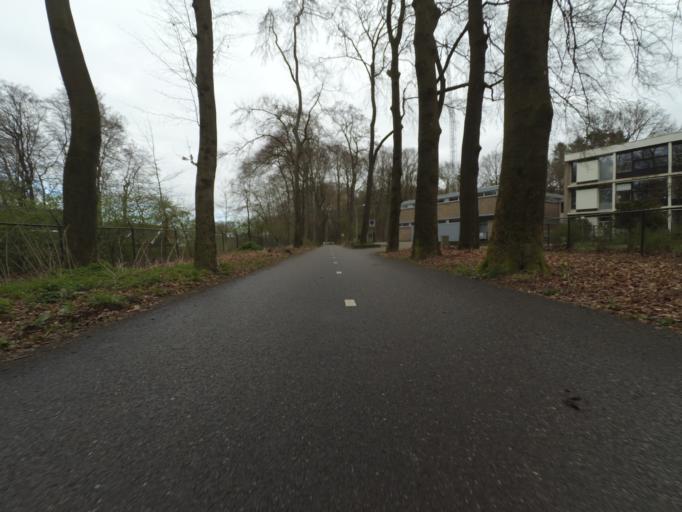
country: NL
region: Gelderland
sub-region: Gemeente Arnhem
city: Burgemeesterswijk
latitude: 52.0091
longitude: 5.9153
